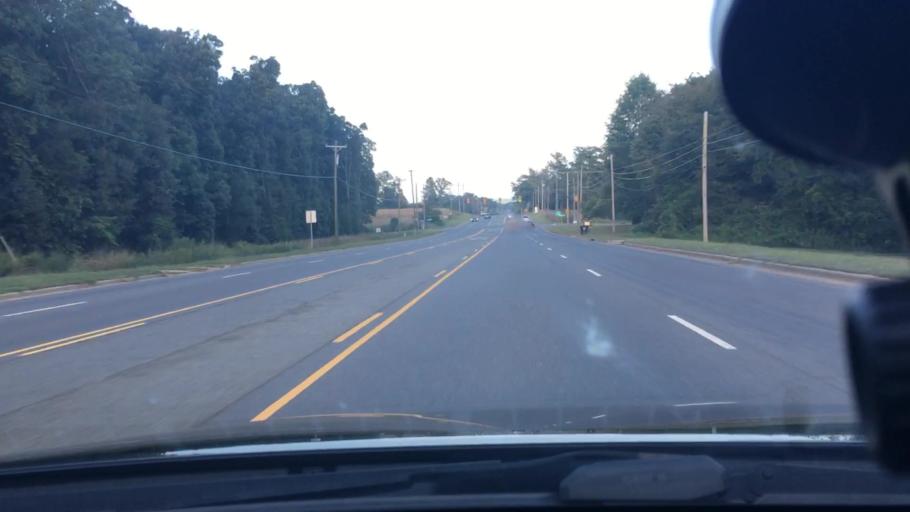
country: US
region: North Carolina
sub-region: Cabarrus County
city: Midland
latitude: 35.2494
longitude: -80.5408
